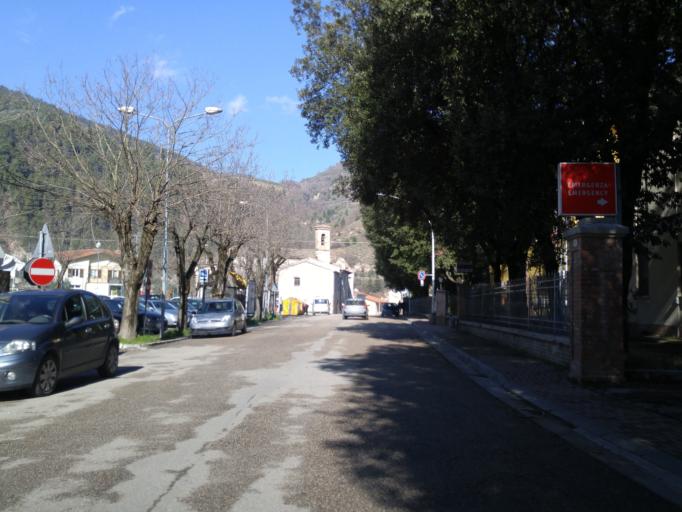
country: IT
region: The Marches
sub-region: Provincia di Pesaro e Urbino
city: Fossombrone
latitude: 43.6854
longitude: 12.8035
